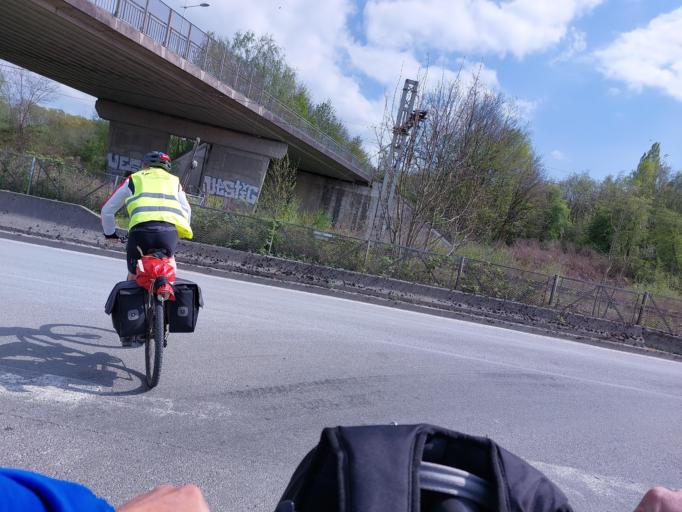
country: FR
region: Nord-Pas-de-Calais
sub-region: Departement du Nord
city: Hautmont
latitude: 50.2467
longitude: 3.9028
